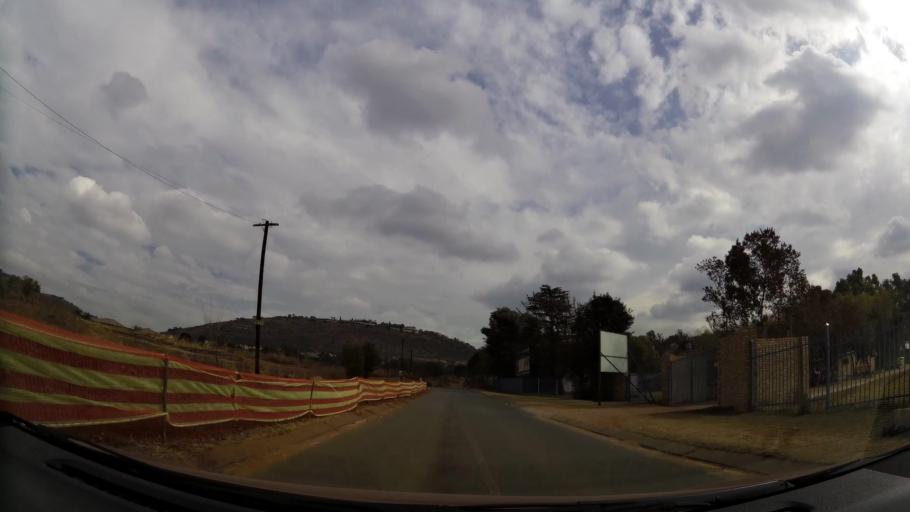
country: ZA
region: Gauteng
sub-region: City of Johannesburg Metropolitan Municipality
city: Roodepoort
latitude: -26.1027
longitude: 27.8810
